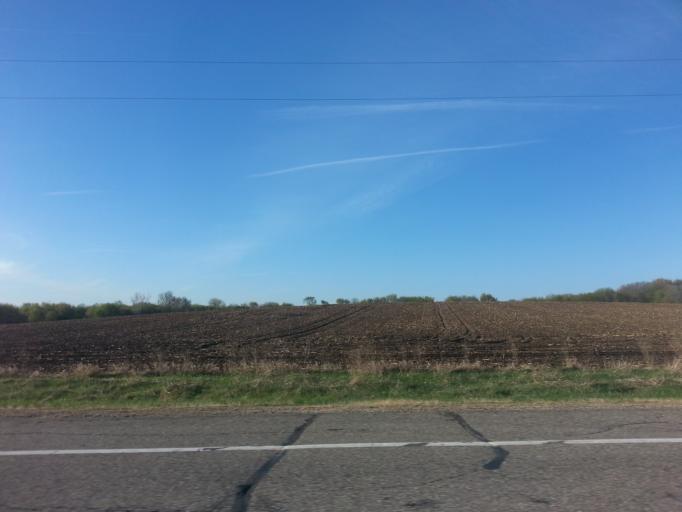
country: US
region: Minnesota
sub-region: Dakota County
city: Lakeville
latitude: 44.5872
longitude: -93.2464
